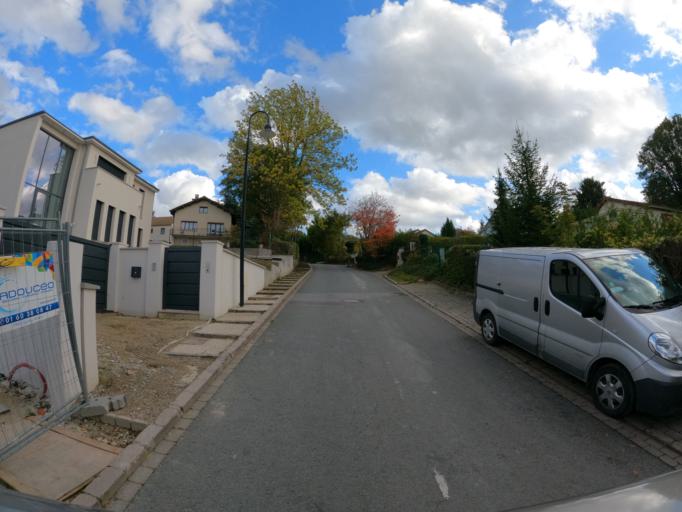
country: FR
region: Ile-de-France
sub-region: Departement de Seine-et-Marne
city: Chessy
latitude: 48.8835
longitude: 2.7629
